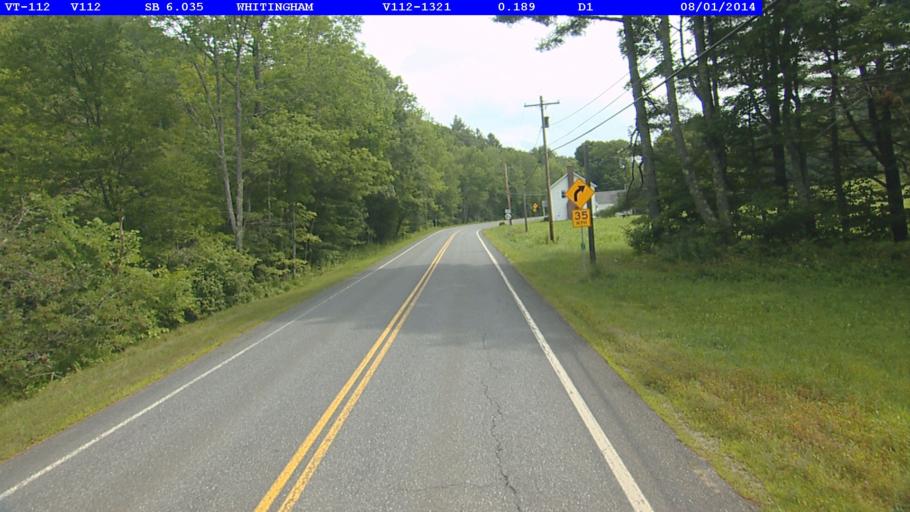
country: US
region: Massachusetts
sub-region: Franklin County
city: Colrain
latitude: 42.7814
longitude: -72.8064
